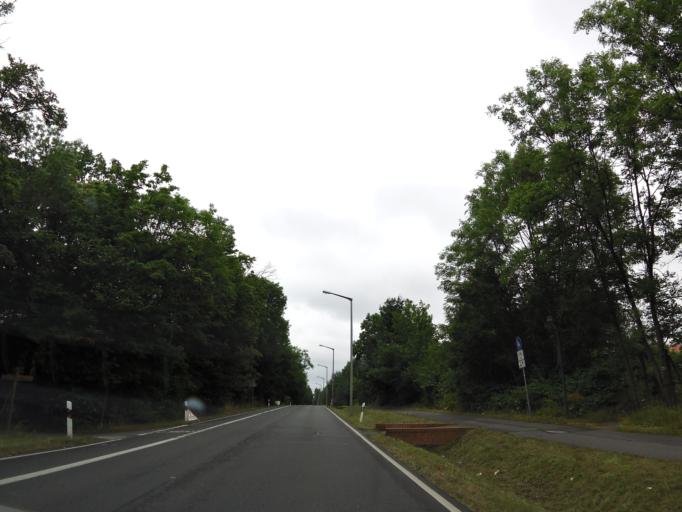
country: DE
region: Saxony
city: Markkleeberg
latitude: 51.2884
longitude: 12.4291
